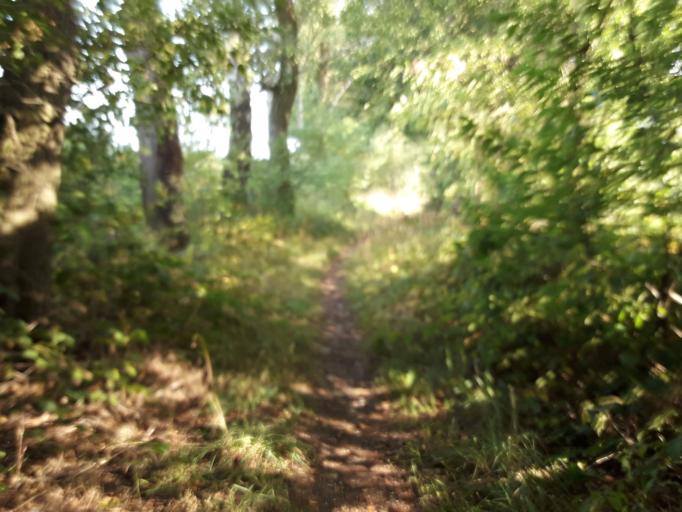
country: DE
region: North Rhine-Westphalia
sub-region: Regierungsbezirk Detmold
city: Hovelhof
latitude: 51.7918
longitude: 8.6734
